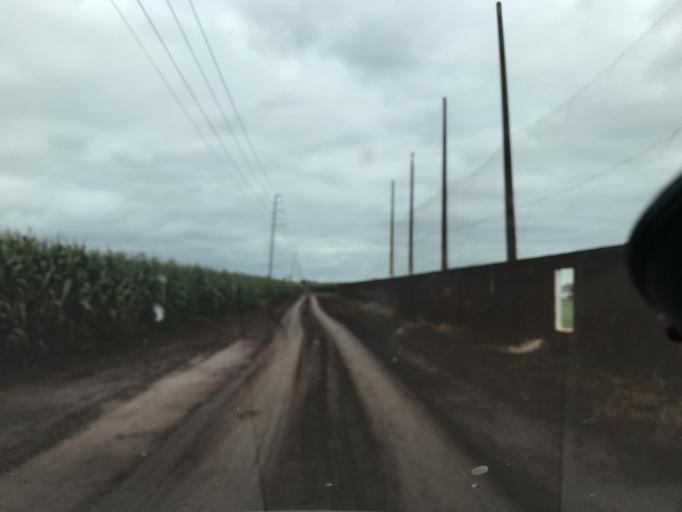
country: BR
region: Parana
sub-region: Palotina
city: Palotina
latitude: -24.3061
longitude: -53.8226
